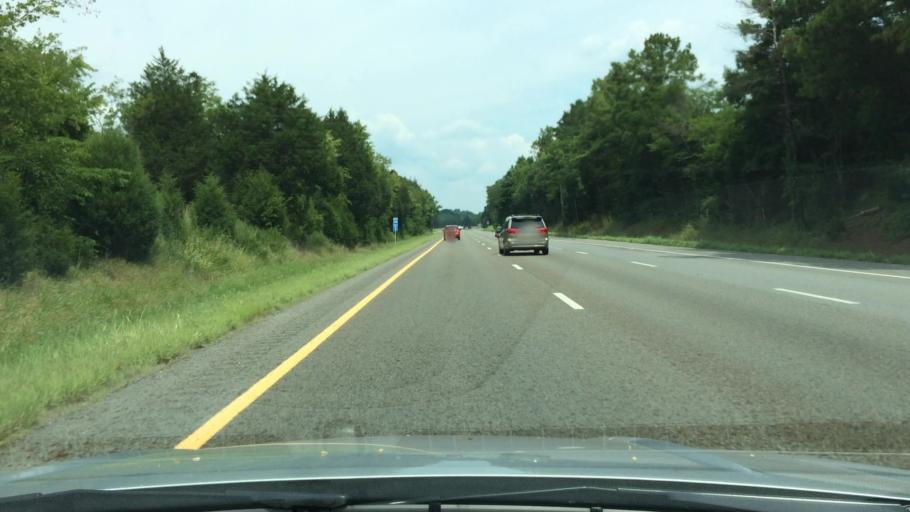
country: US
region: Tennessee
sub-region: Marshall County
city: Lewisburg
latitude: 35.4528
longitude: -86.8846
